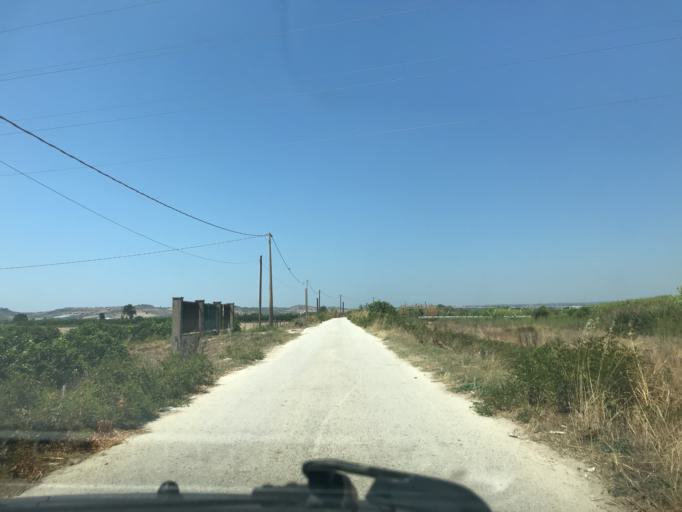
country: IT
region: Sicily
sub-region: Provincia di Siracusa
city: Noto
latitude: 36.8364
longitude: 15.0567
